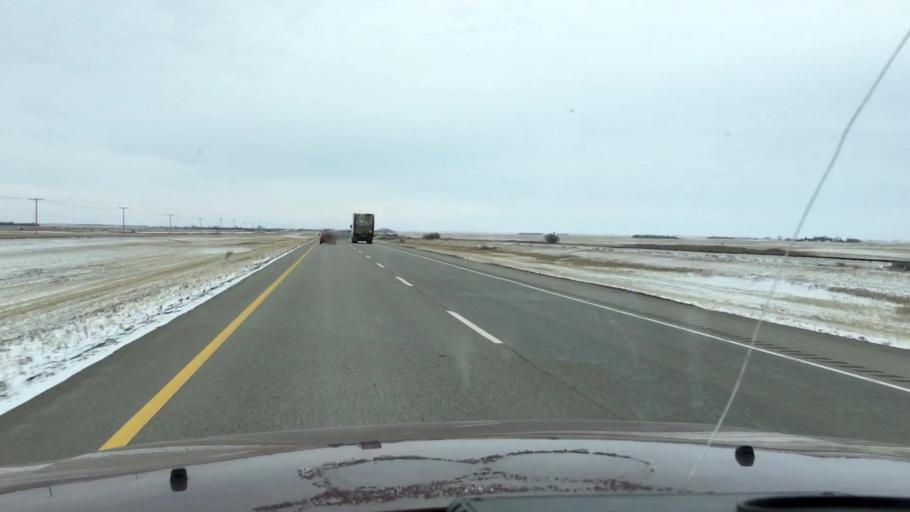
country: CA
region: Saskatchewan
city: Watrous
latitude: 51.1878
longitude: -105.9459
